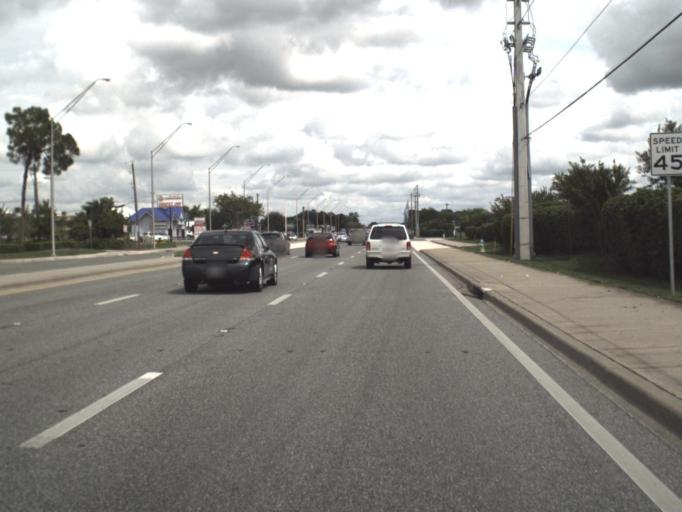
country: US
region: Florida
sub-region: Sarasota County
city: Bee Ridge
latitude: 27.2692
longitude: -82.4884
